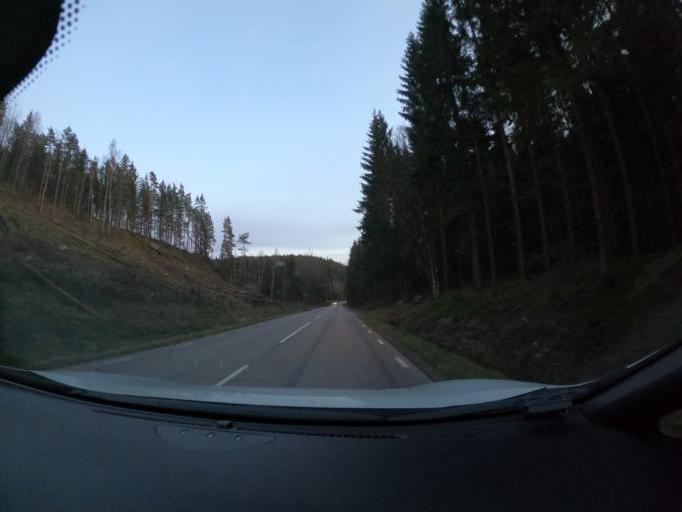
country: SE
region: Vaestra Goetaland
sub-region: Harryda Kommun
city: Landvetter
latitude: 57.6268
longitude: 12.1812
